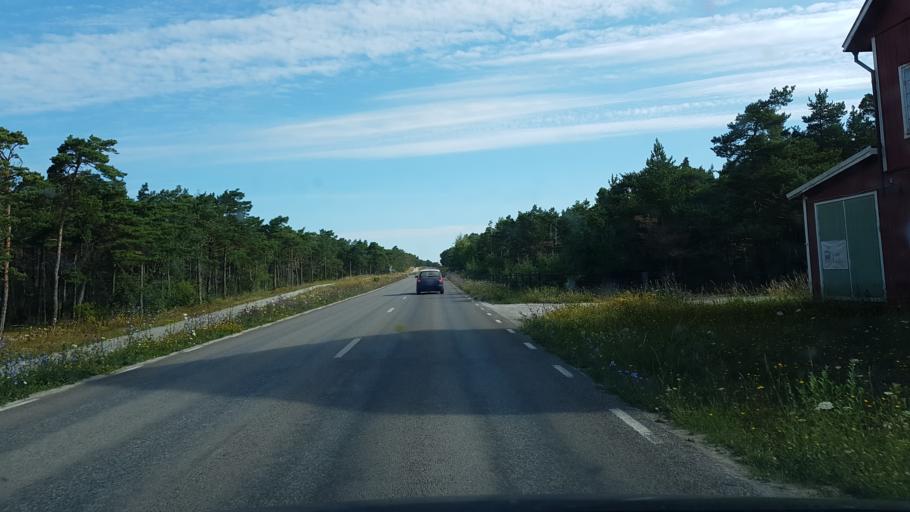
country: SE
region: Gotland
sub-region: Gotland
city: Visby
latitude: 57.7020
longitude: 18.3793
